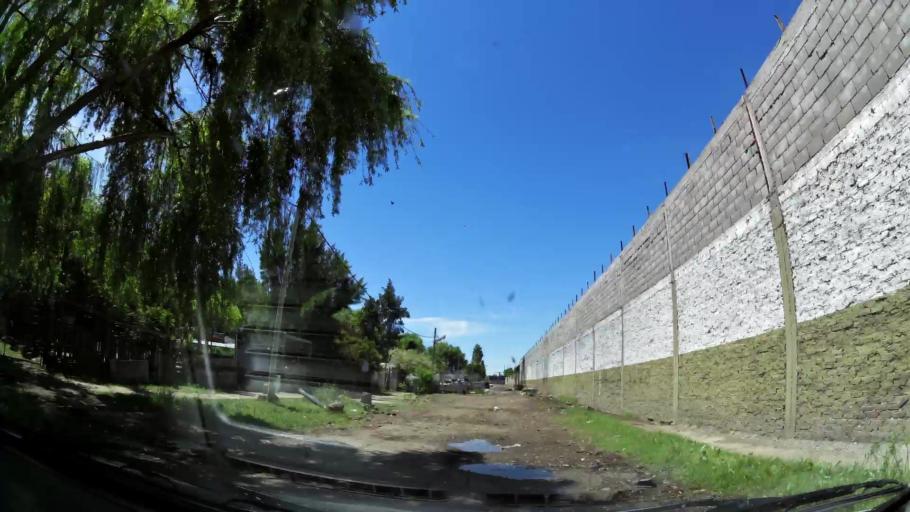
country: AR
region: Buenos Aires
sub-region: Partido de Quilmes
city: Quilmes
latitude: -34.7500
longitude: -58.3099
